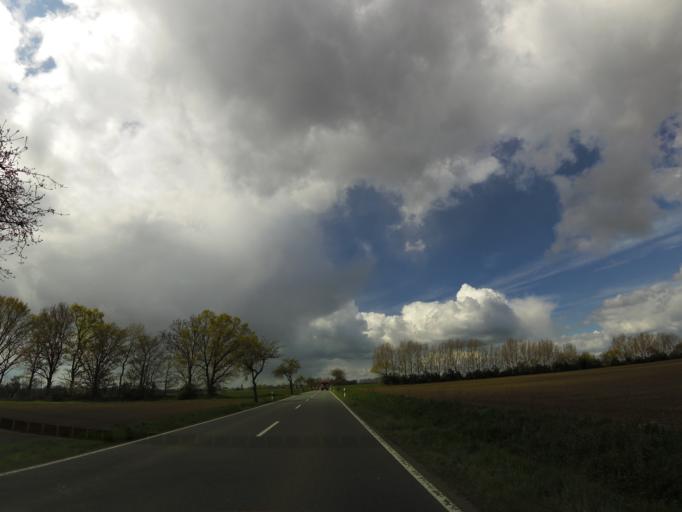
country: DE
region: Saxony-Anhalt
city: Hohendodeleben
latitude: 52.0778
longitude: 11.5076
